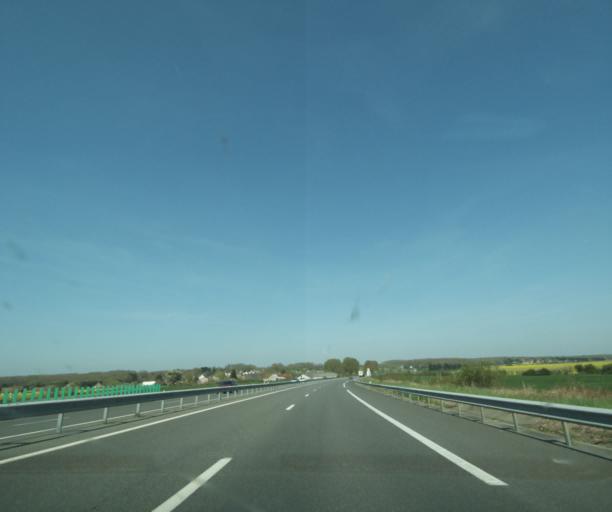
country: FR
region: Bourgogne
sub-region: Departement de la Nievre
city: Pouilly-sur-Loire
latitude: 47.3286
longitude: 2.9307
